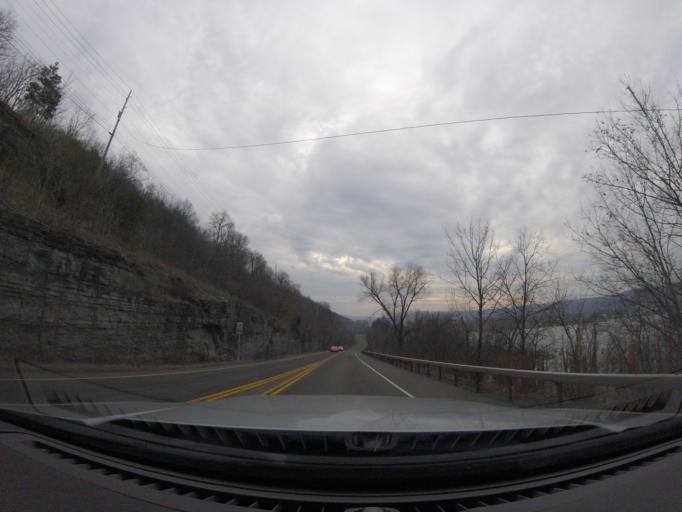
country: US
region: New York
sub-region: Schuyler County
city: Watkins Glen
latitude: 42.3932
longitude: -76.8564
